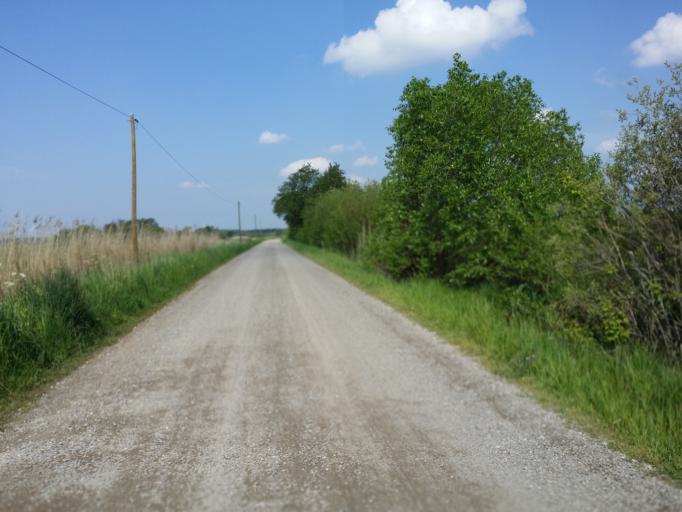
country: DE
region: Lower Saxony
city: Osterholz-Scharmbeck
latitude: 53.2186
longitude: 8.8532
